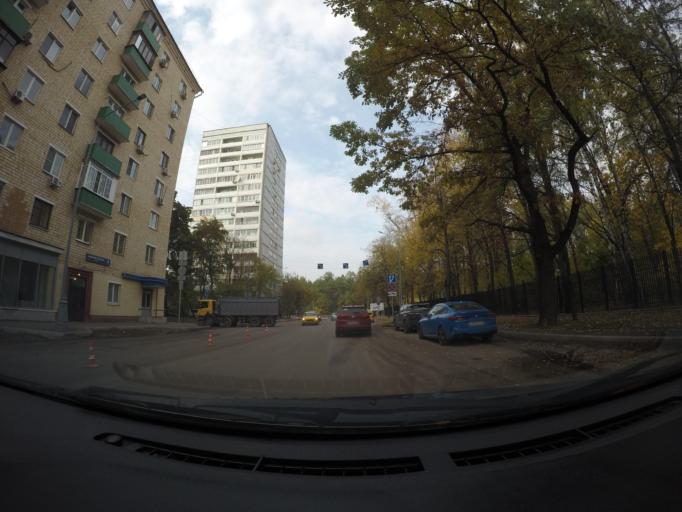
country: RU
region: Moskovskaya
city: Izmaylovo
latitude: 55.7646
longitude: 37.7907
